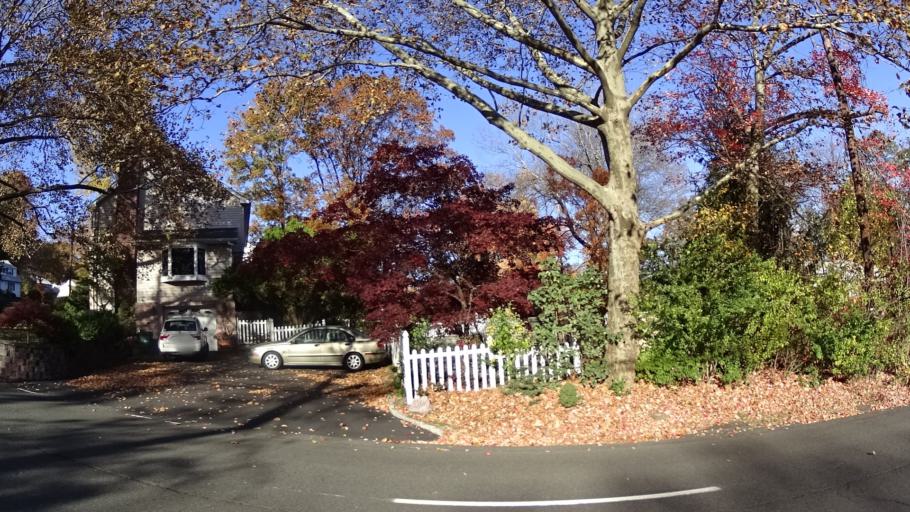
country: US
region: New Jersey
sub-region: Union County
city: Mountainside
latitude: 40.6873
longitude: -74.3500
